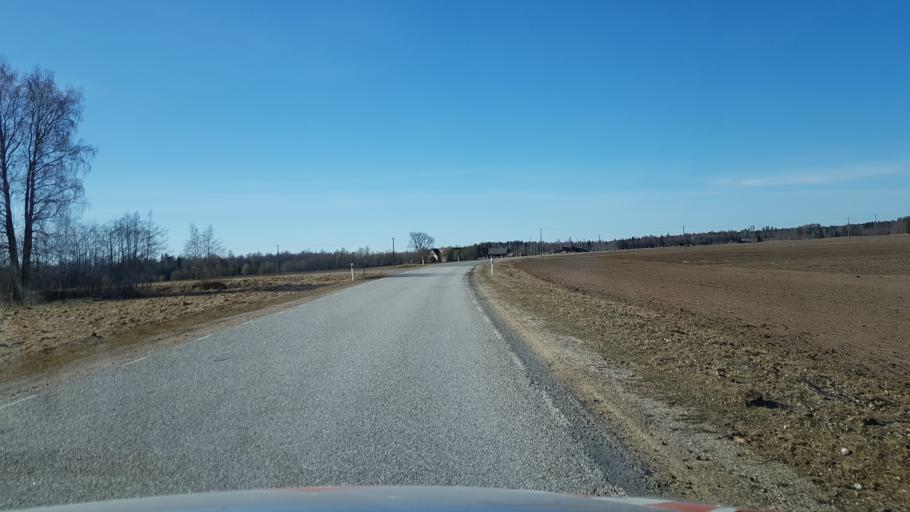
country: EE
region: Laeaene-Virumaa
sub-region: Vinni vald
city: Vinni
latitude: 59.2332
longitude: 26.6988
